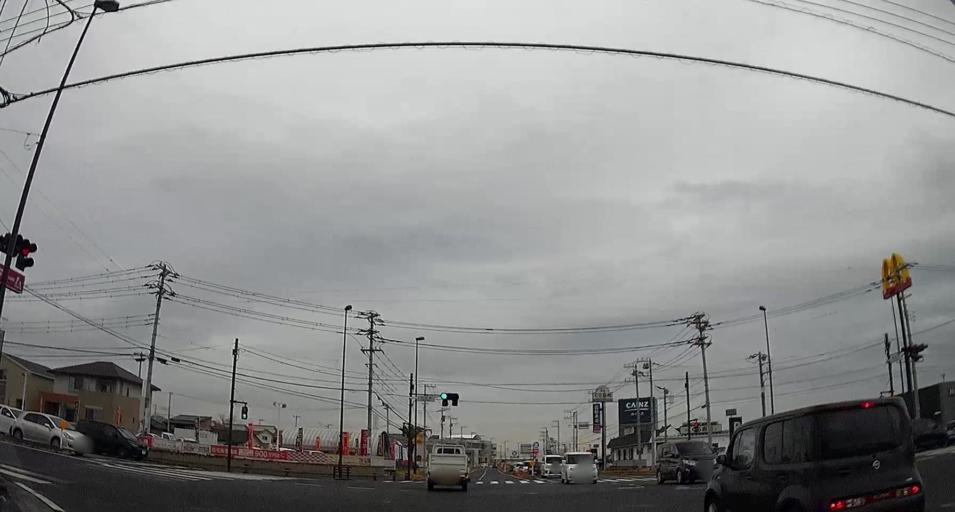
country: JP
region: Chiba
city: Kisarazu
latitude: 35.4309
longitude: 139.9336
